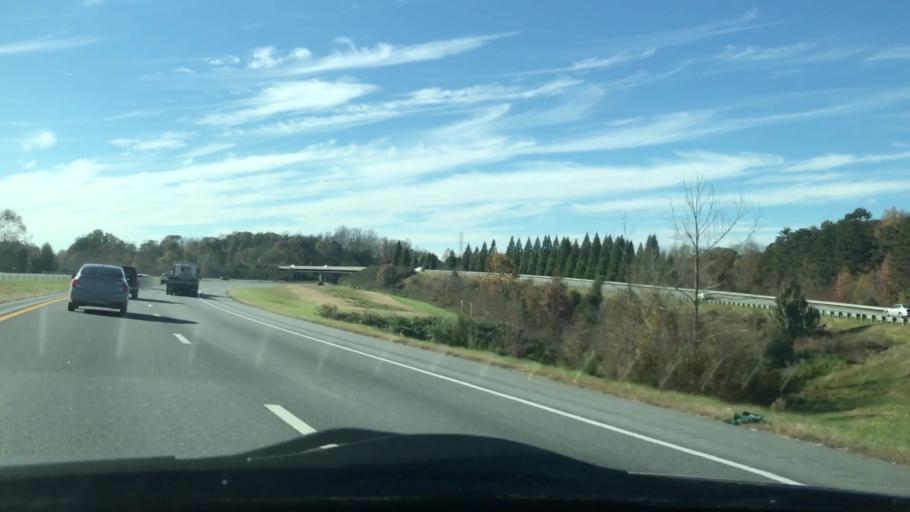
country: US
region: North Carolina
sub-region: Guilford County
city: High Point
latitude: 36.0076
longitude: -80.0266
